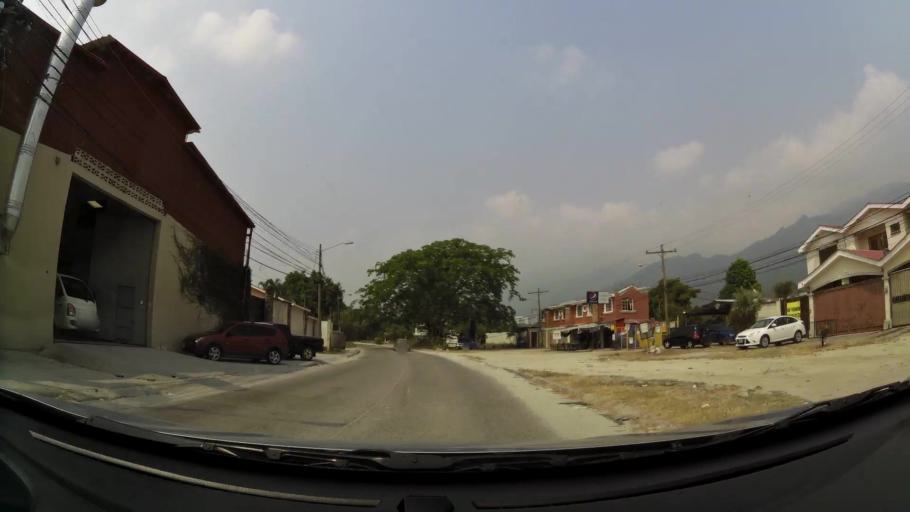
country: HN
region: Cortes
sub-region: San Pedro Sula
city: Pena Blanca
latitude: 15.5476
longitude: -88.0276
